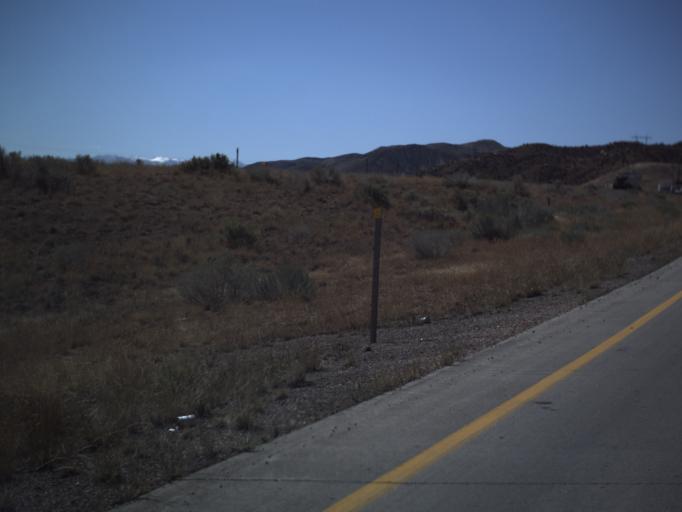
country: US
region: Utah
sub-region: Sevier County
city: Richfield
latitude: 38.7896
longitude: -112.0855
